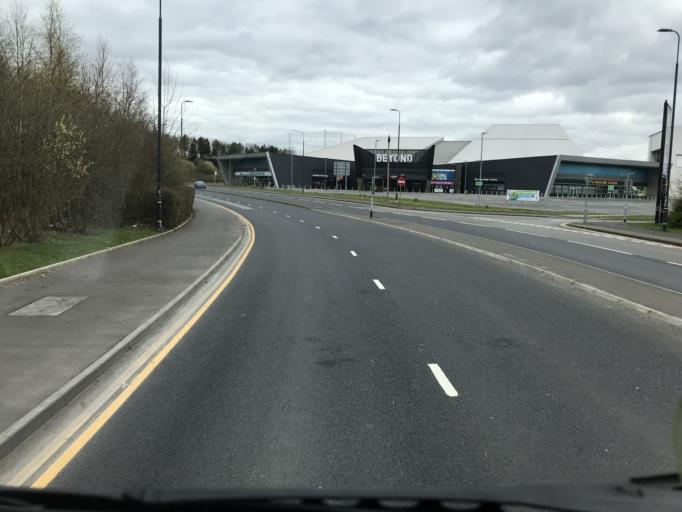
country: GB
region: England
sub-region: Trafford
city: Urmston
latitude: 53.4698
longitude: -2.3628
